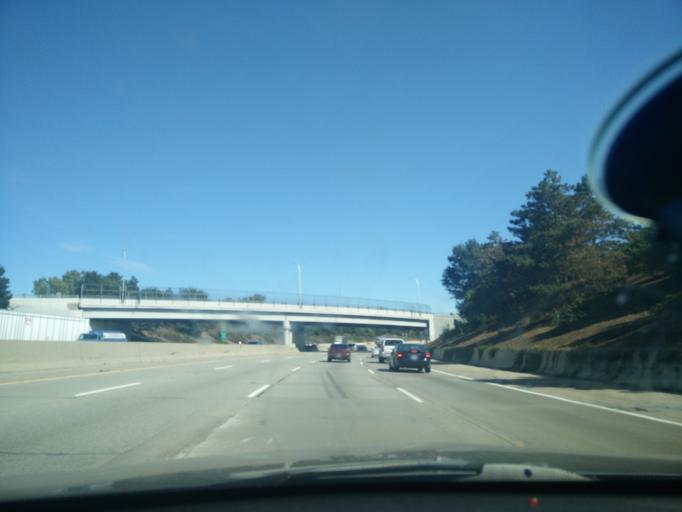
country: US
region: Michigan
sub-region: Oakland County
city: Madison Heights
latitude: 42.4894
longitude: -83.0802
